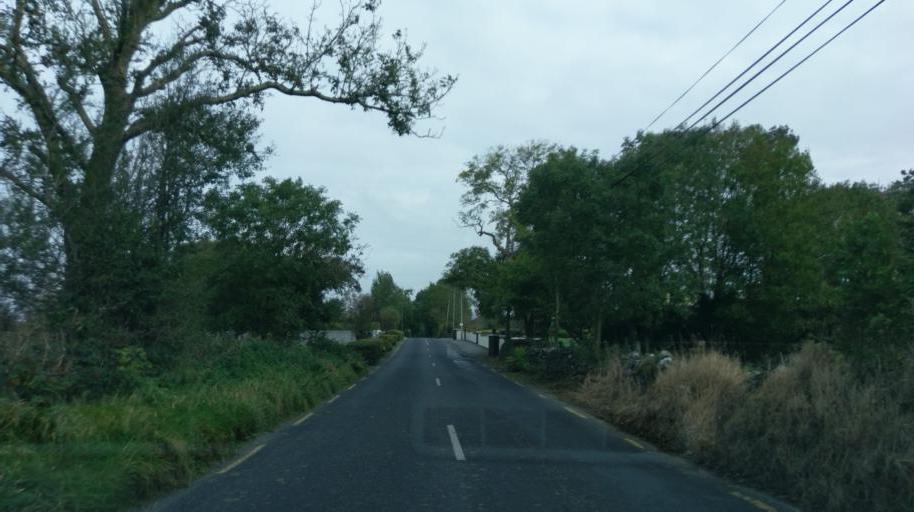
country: IE
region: Connaught
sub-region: County Galway
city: Athenry
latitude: 53.3638
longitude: -8.7016
